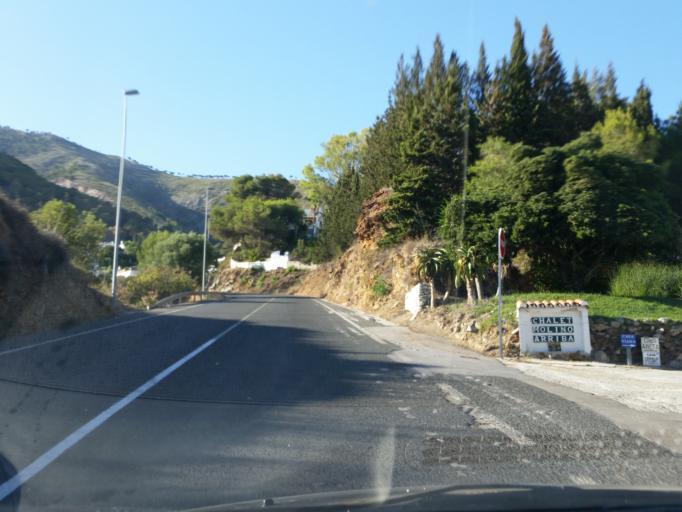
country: ES
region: Andalusia
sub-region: Provincia de Malaga
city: Mijas
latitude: 36.5965
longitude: -4.6320
